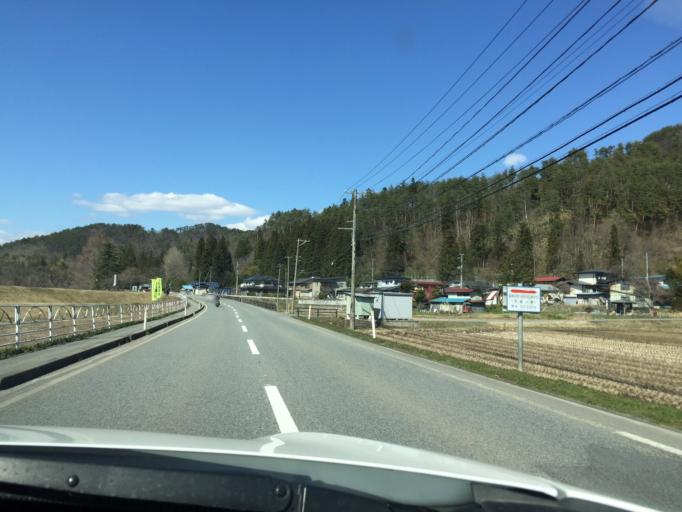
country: JP
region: Yamagata
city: Nagai
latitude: 38.1973
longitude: 140.1031
